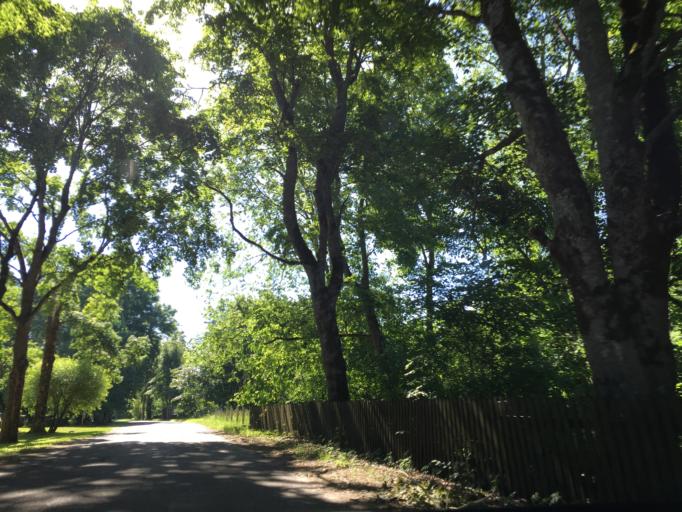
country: LV
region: Ventspils Rajons
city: Piltene
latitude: 57.3271
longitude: 22.0161
